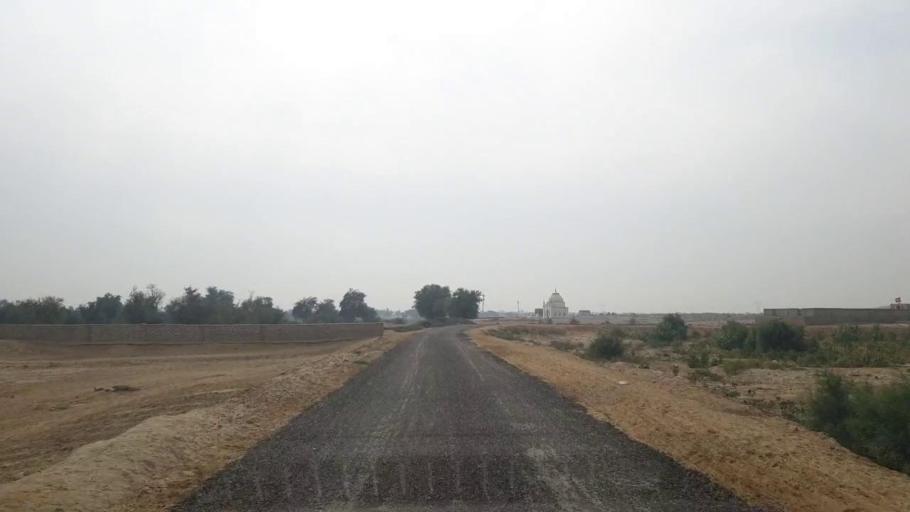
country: PK
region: Sindh
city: Sann
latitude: 25.9662
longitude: 68.1469
